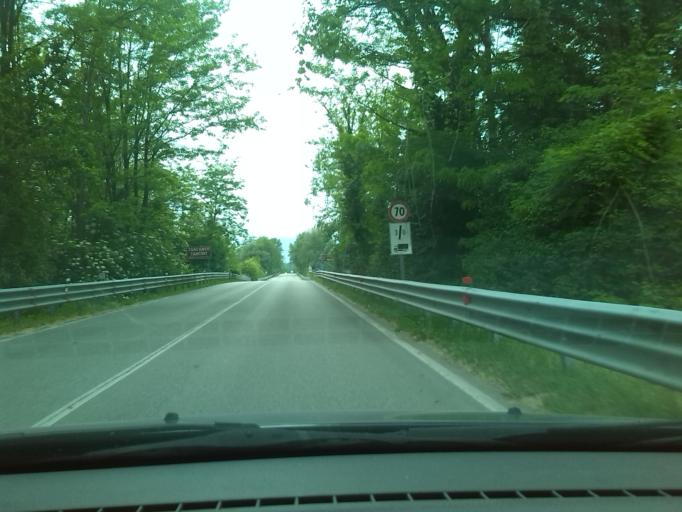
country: IT
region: Friuli Venezia Giulia
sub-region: Provincia di Udine
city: Magnano in Riviera
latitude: 46.2179
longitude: 13.1950
